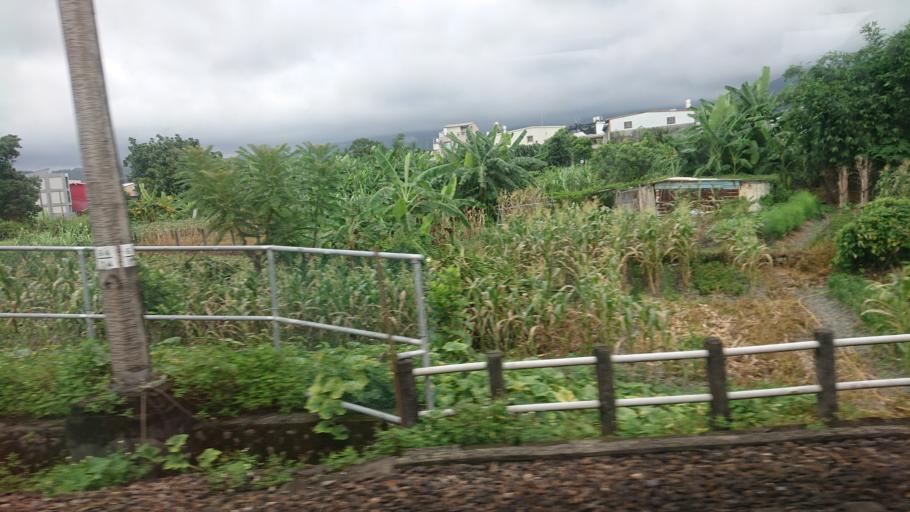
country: TW
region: Taiwan
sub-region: Yilan
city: Yilan
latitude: 24.8159
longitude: 121.7701
